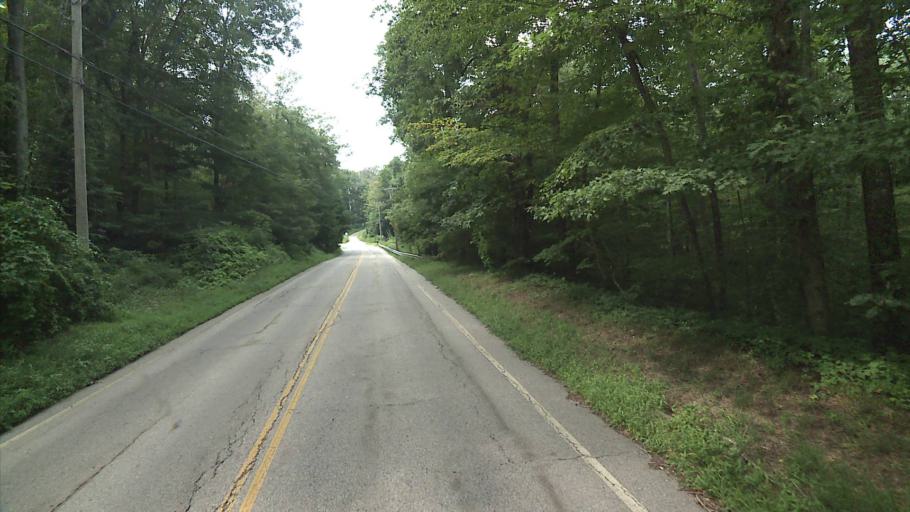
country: US
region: Connecticut
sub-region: Middlesex County
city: Essex Village
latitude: 41.4310
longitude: -72.3579
